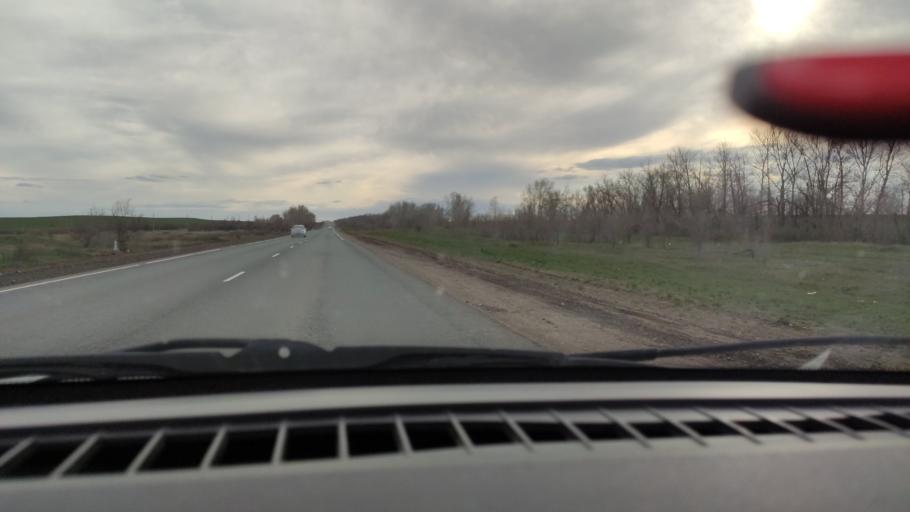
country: RU
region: Orenburg
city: Sakmara
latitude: 52.3087
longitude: 55.4514
